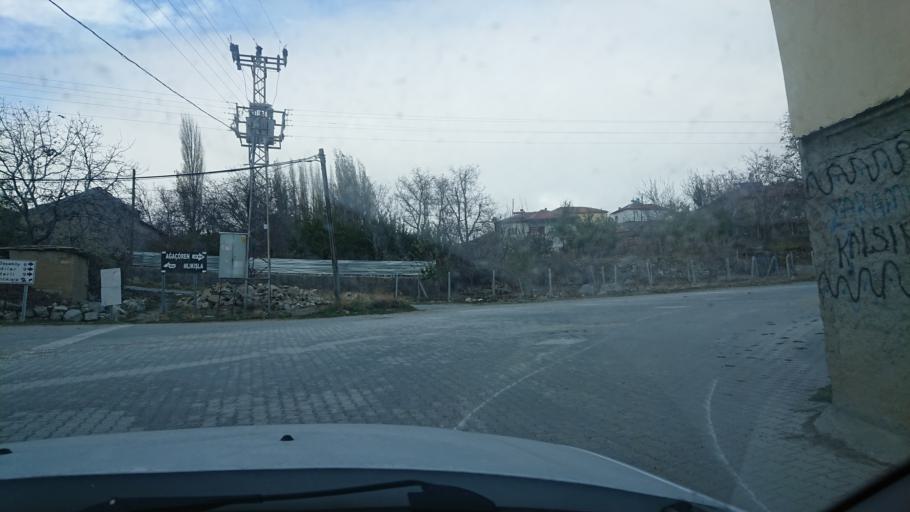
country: TR
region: Aksaray
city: Ortakoy
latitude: 38.7587
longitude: 34.0104
